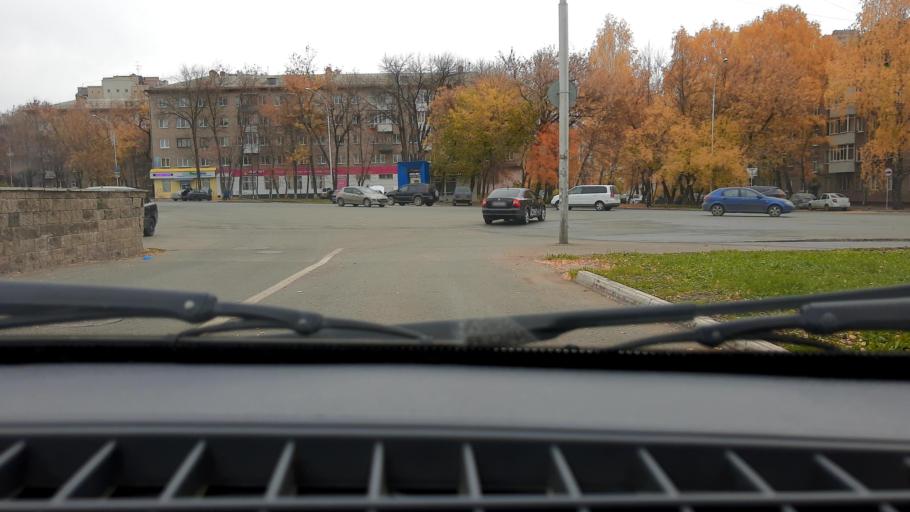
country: RU
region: Bashkortostan
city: Ufa
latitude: 54.8155
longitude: 56.0907
